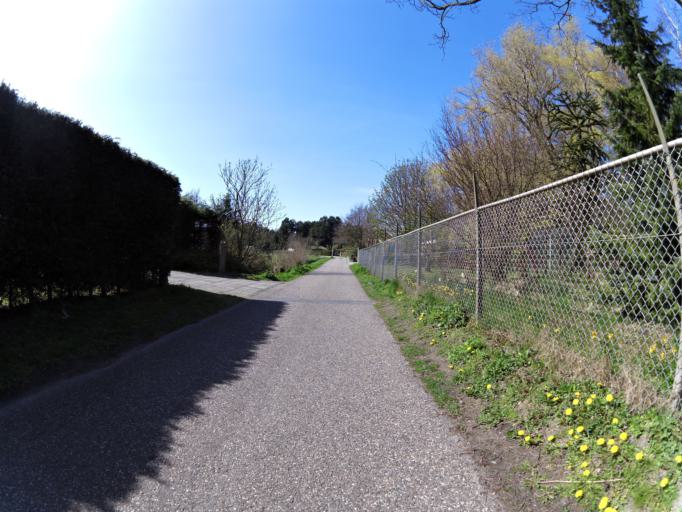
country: NL
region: South Holland
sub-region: Gemeente Brielle
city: Brielle
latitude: 51.9075
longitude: 4.1043
